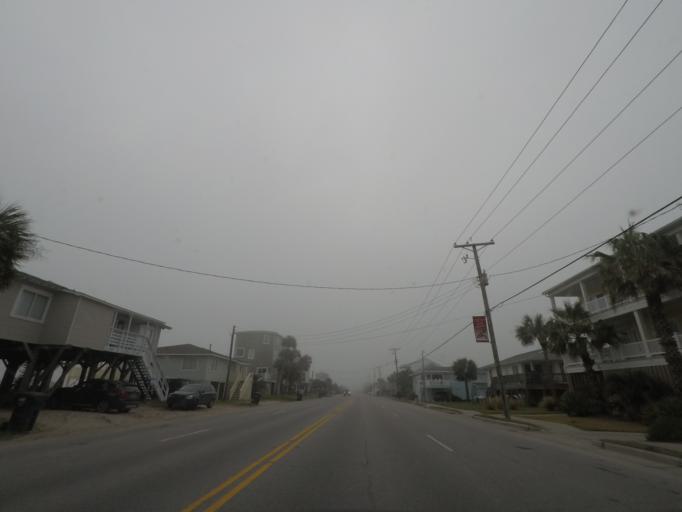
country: US
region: South Carolina
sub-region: Charleston County
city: Seabrook Island
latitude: 32.4980
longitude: -80.3045
